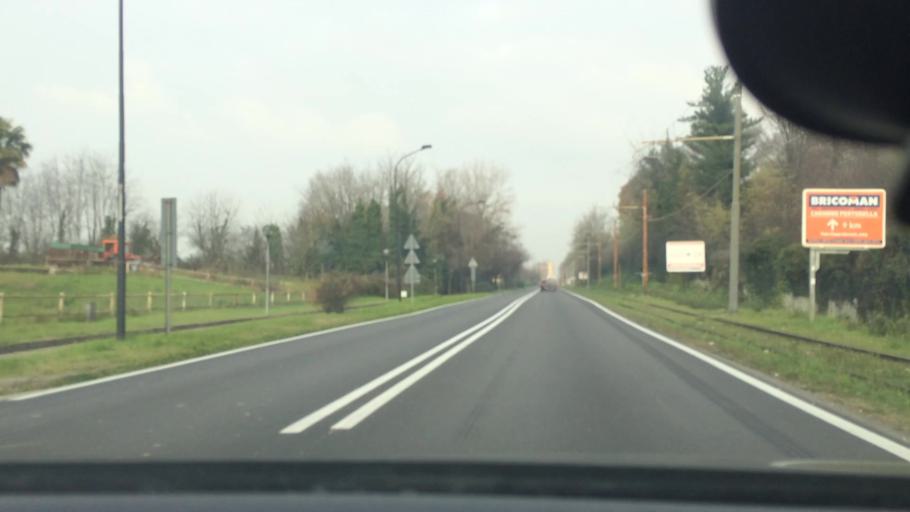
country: IT
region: Lombardy
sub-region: Provincia di Monza e Brianza
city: Limbiate
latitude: 45.6084
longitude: 9.1217
